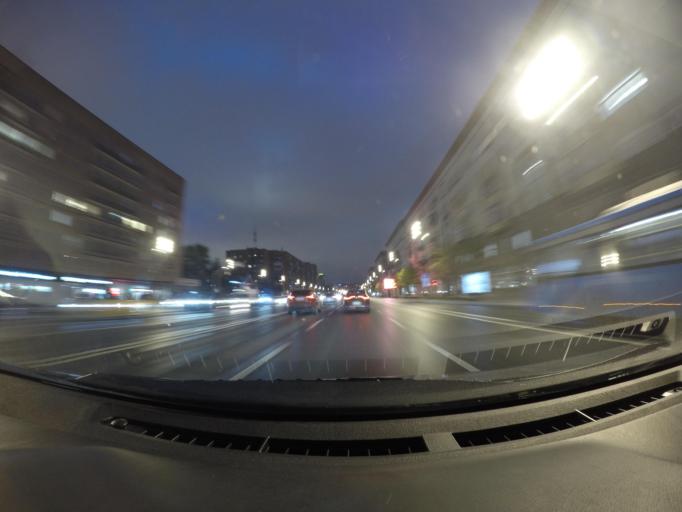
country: RU
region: Moskovskaya
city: Dorogomilovo
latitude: 55.7464
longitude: 37.5592
